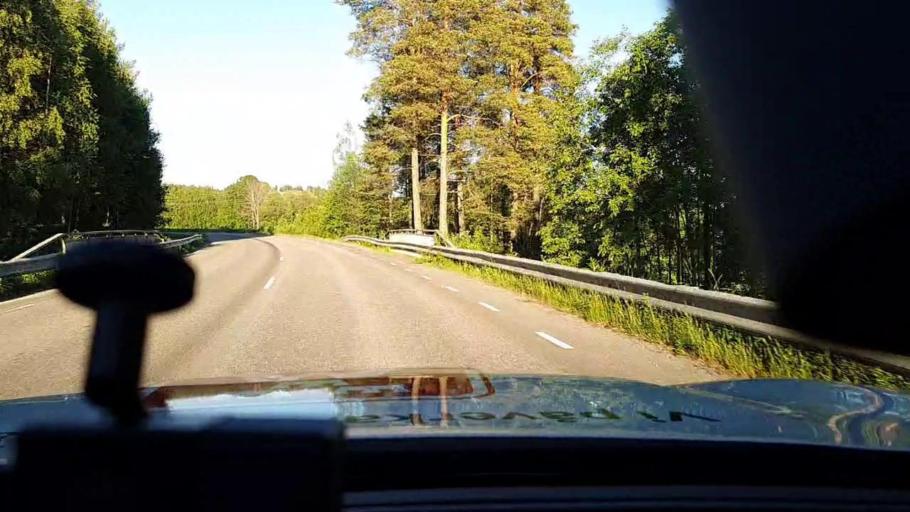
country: SE
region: Norrbotten
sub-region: Lulea Kommun
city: Lulea
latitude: 65.6074
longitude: 22.1710
